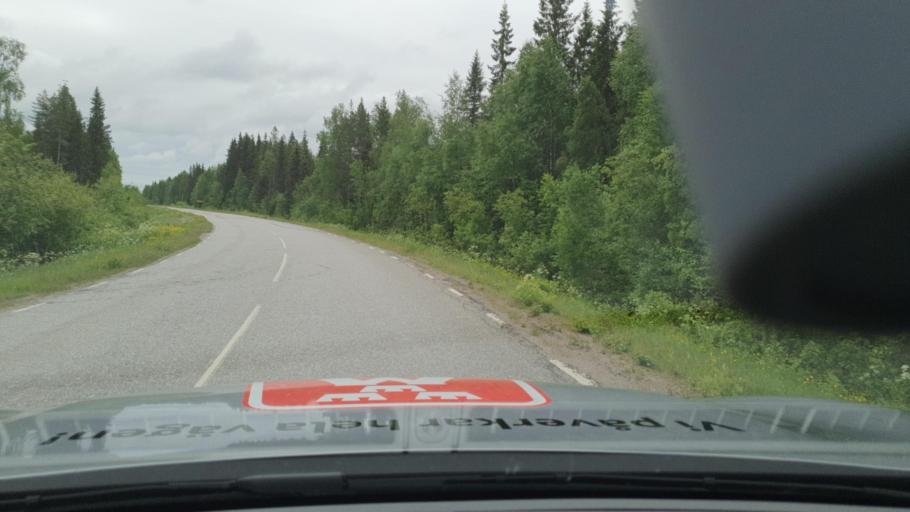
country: SE
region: Norrbotten
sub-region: Lulea Kommun
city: Ranea
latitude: 65.8557
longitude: 22.2353
